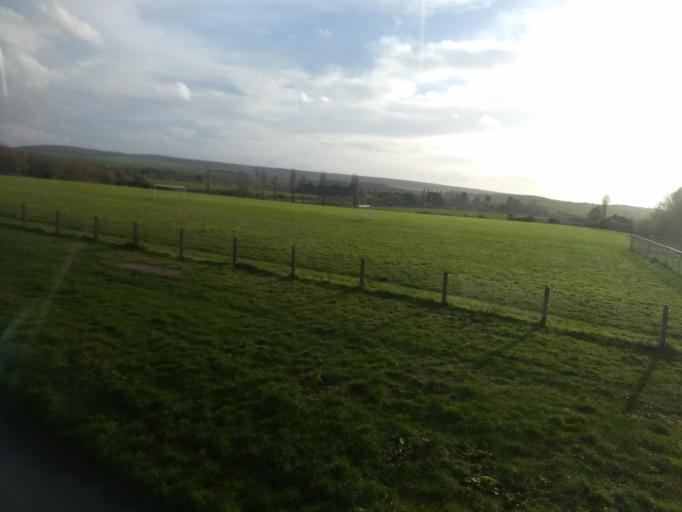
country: GB
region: England
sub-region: Isle of Wight
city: Yarmouth
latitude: 50.7069
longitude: -1.4787
